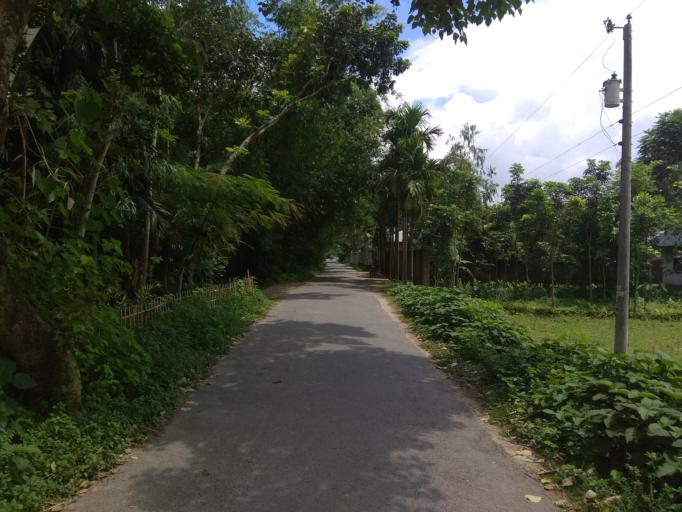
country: IN
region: West Bengal
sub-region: Koch Bihar
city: Haldibari
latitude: 26.1637
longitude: 88.9240
